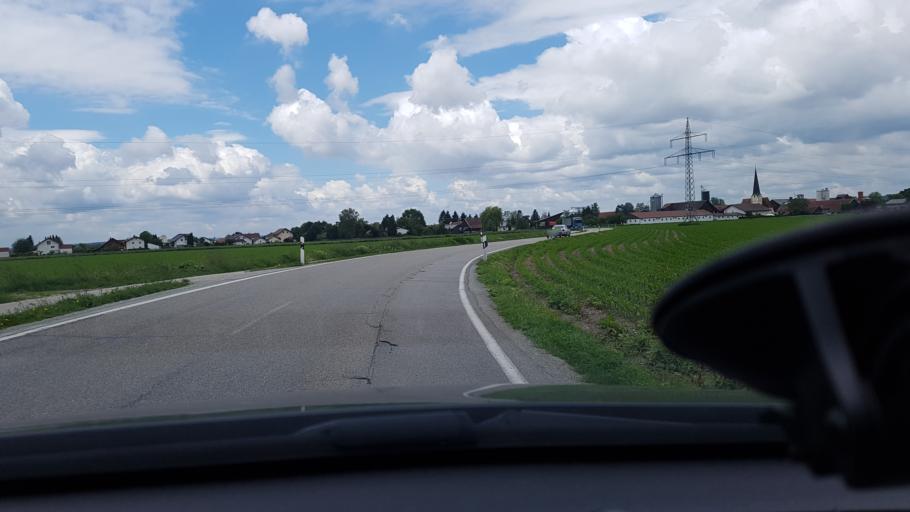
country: DE
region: Bavaria
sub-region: Lower Bavaria
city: Pocking
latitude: 48.4062
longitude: 13.3537
